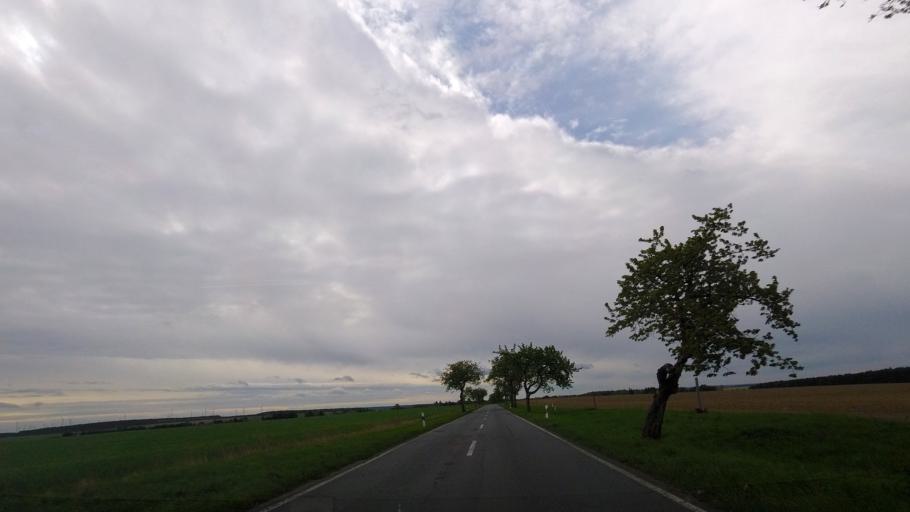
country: DE
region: Brandenburg
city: Dahme
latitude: 51.9107
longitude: 13.4023
